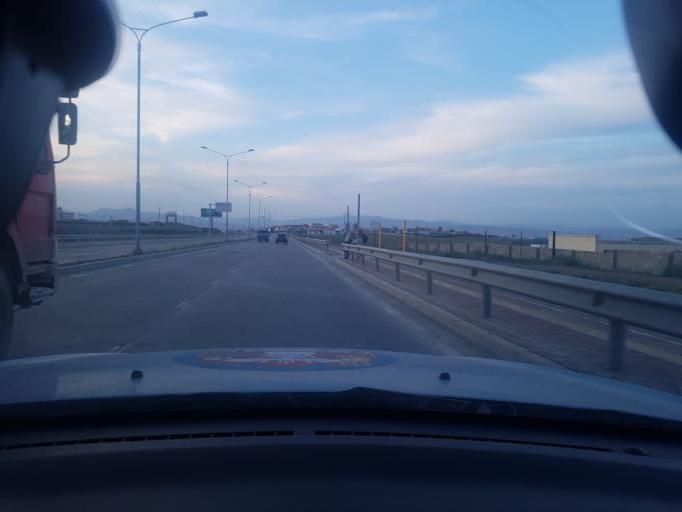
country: MN
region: Ulaanbaatar
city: Ulaanbaatar
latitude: 47.8594
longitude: 106.7880
